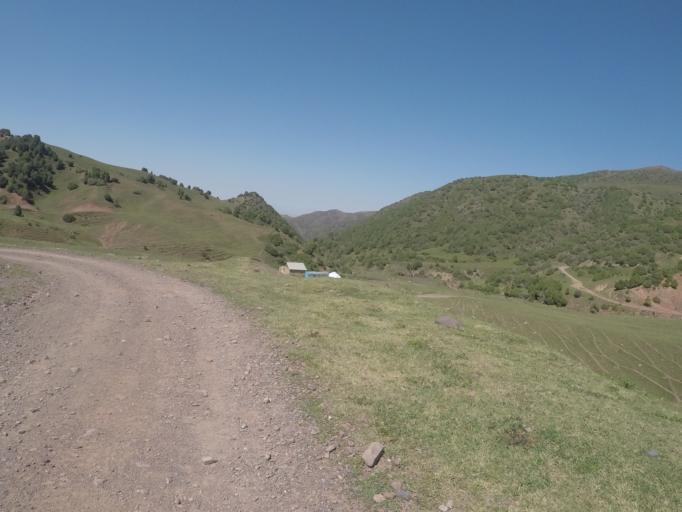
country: KG
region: Chuy
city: Bishkek
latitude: 42.6456
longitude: 74.5743
